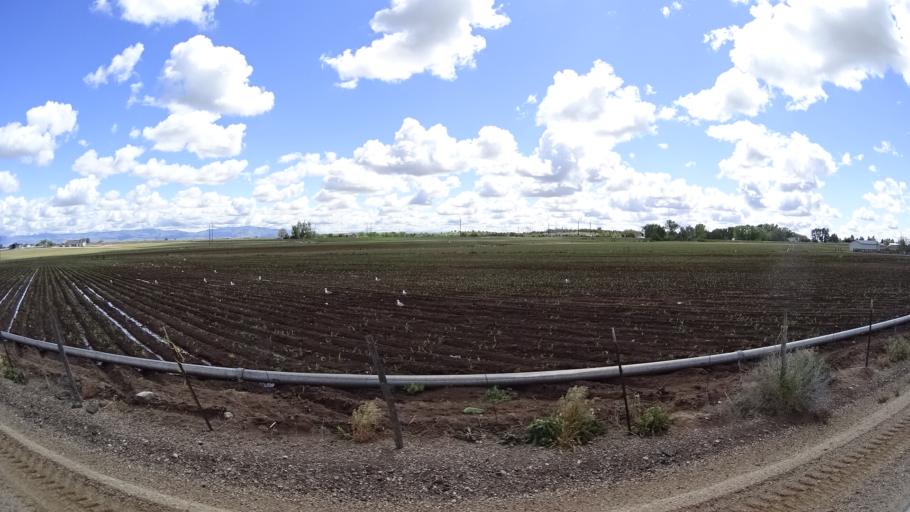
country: US
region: Idaho
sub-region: Ada County
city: Kuna
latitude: 43.5088
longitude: -116.3445
